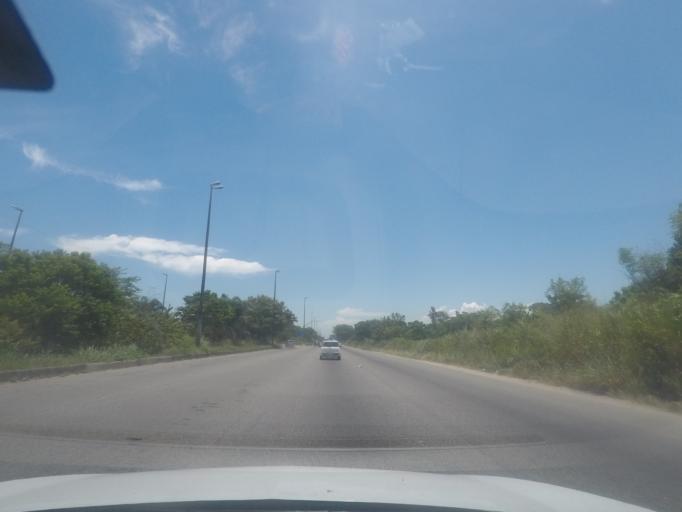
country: BR
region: Rio de Janeiro
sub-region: Itaguai
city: Itaguai
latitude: -22.8888
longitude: -43.6604
